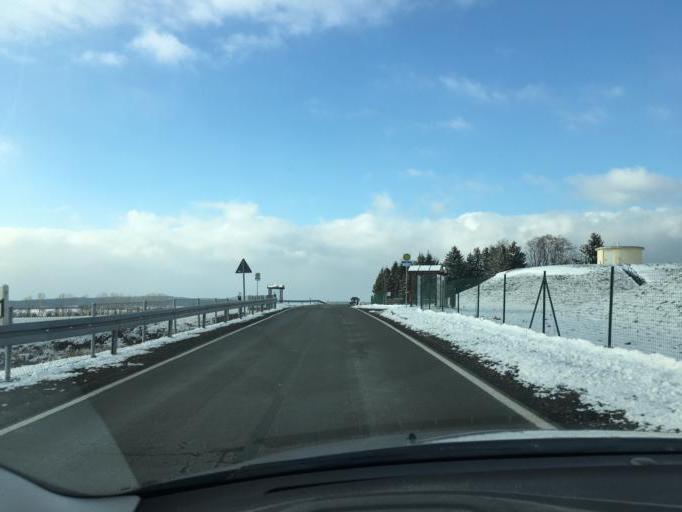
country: DE
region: Saxony
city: Grimma
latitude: 51.2493
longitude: 12.7053
